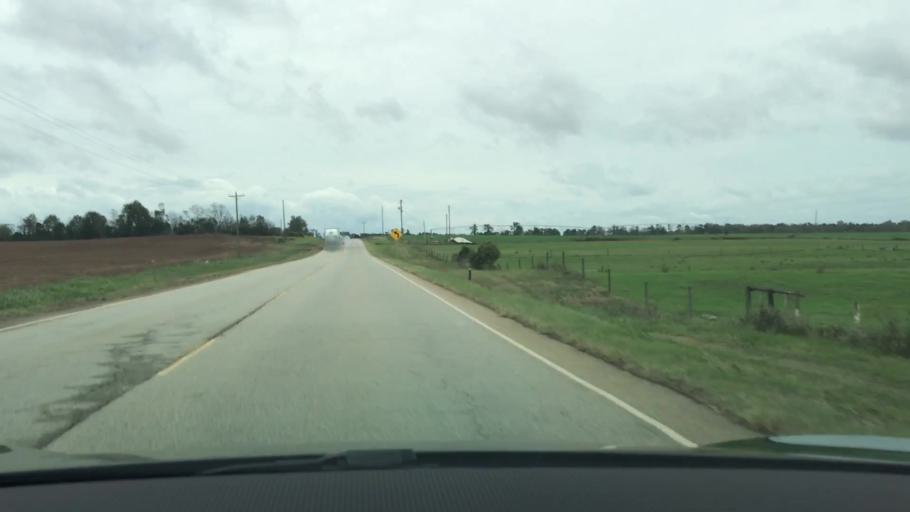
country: US
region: Georgia
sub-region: Jefferson County
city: Louisville
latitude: 33.0812
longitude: -82.4129
